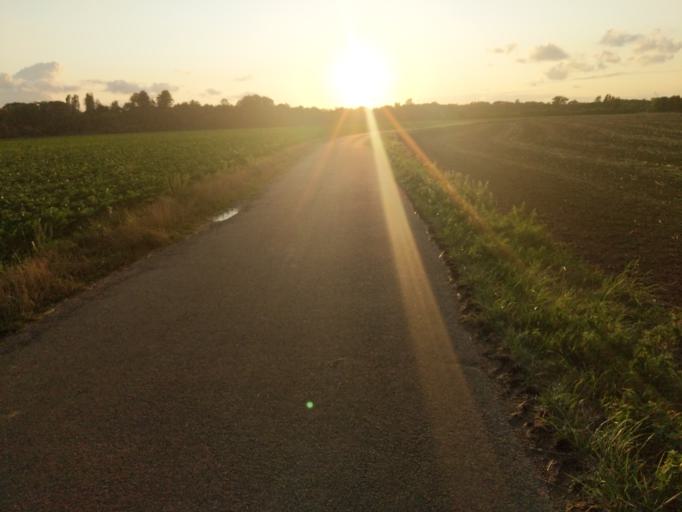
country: DE
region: North Rhine-Westphalia
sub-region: Regierungsbezirk Dusseldorf
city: Krefeld
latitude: 51.3219
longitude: 6.6425
